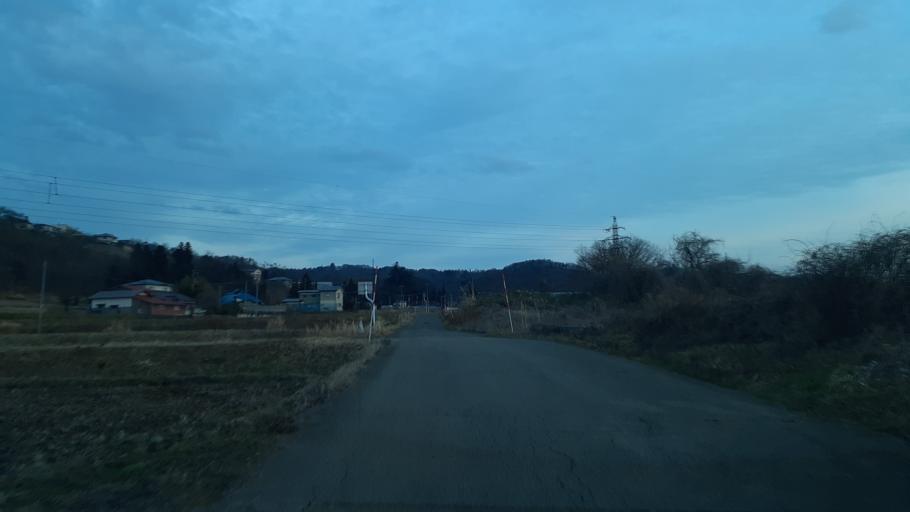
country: JP
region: Fukushima
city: Kitakata
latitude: 37.5273
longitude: 139.9506
